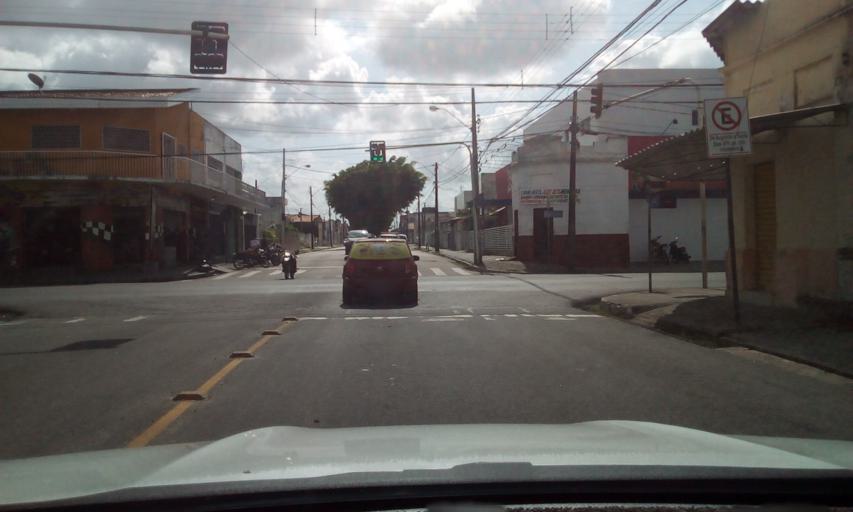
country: BR
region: Paraiba
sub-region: Joao Pessoa
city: Joao Pessoa
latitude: -7.1302
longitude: -34.8786
